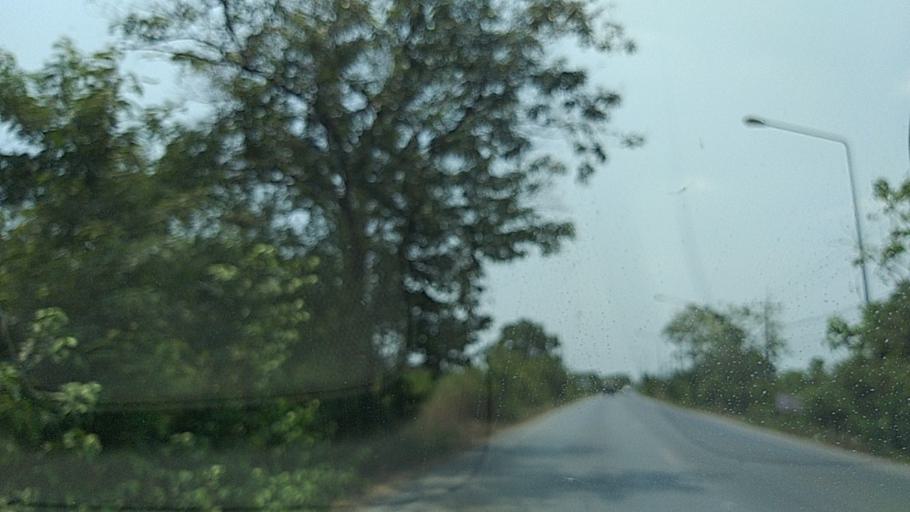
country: TH
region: Chachoengsao
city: Bang Nam Priao
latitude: 13.9390
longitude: 100.9783
